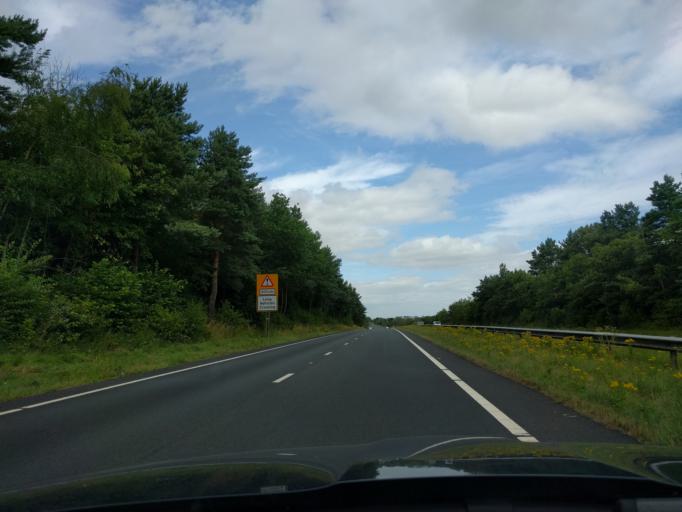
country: GB
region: England
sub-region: Northumberland
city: Felton
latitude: 55.3200
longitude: -1.7248
